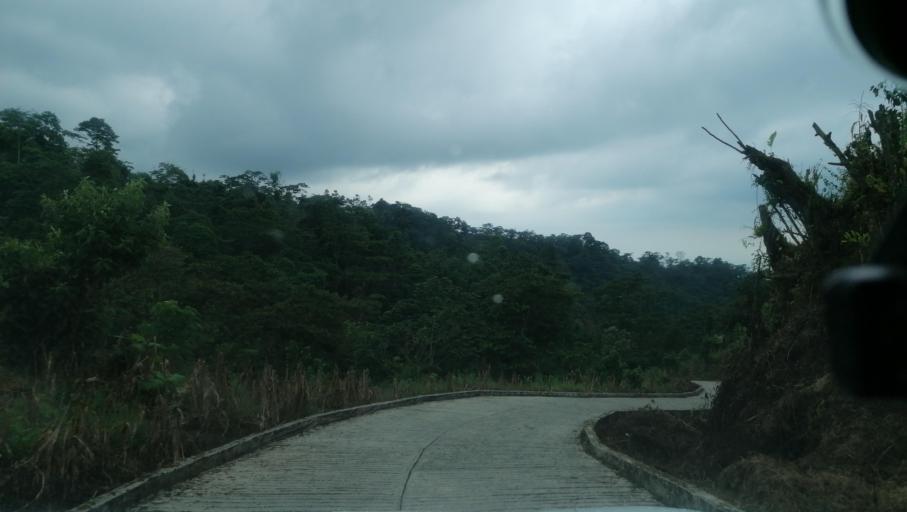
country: MX
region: Chiapas
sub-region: Cacahoatan
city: Benito Juarez
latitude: 15.0919
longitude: -92.1603
